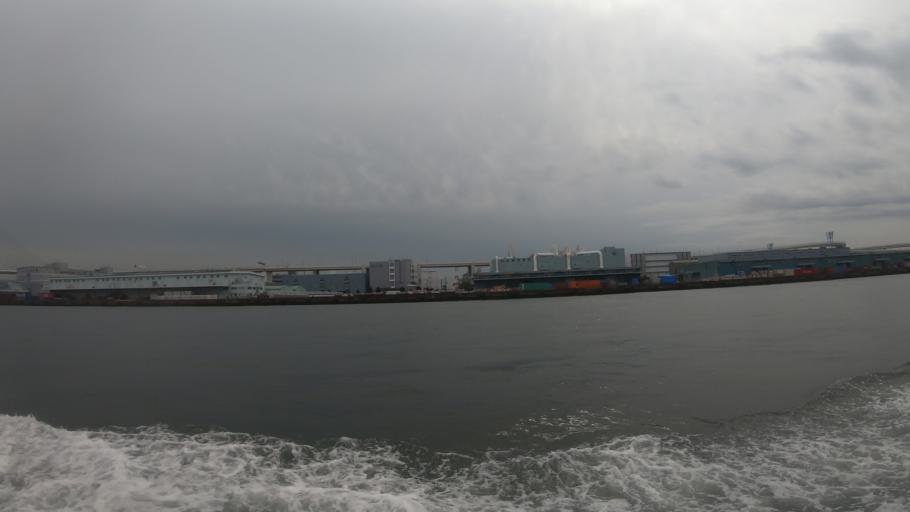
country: JP
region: Kanagawa
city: Yokohama
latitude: 35.4719
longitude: 139.6864
